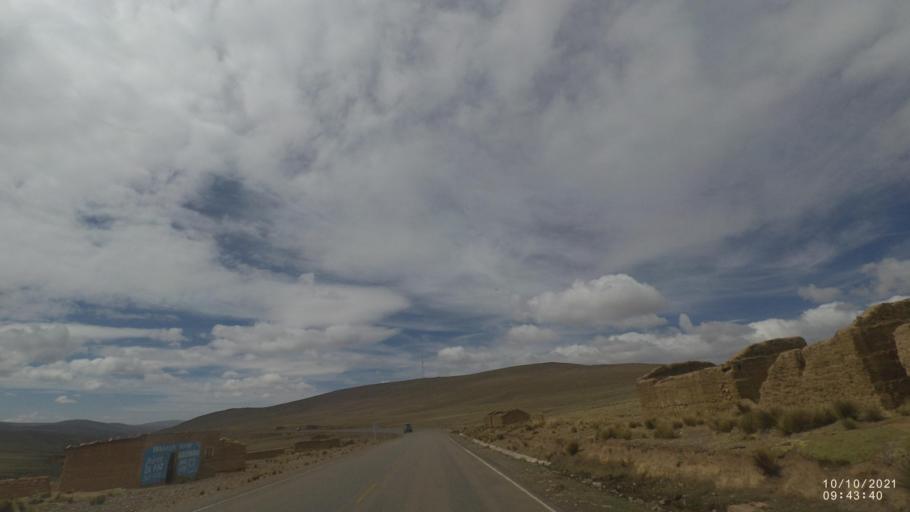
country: BO
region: La Paz
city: Quime
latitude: -17.1523
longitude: -67.3444
